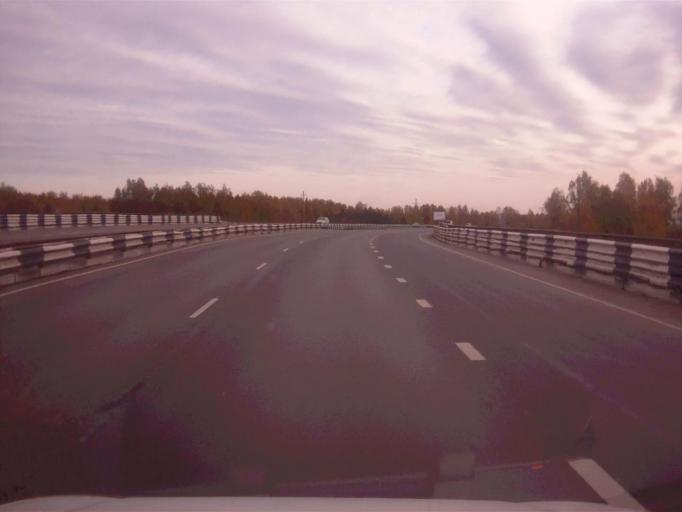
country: RU
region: Chelyabinsk
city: Novosineglazovskiy
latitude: 55.0396
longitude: 61.4396
